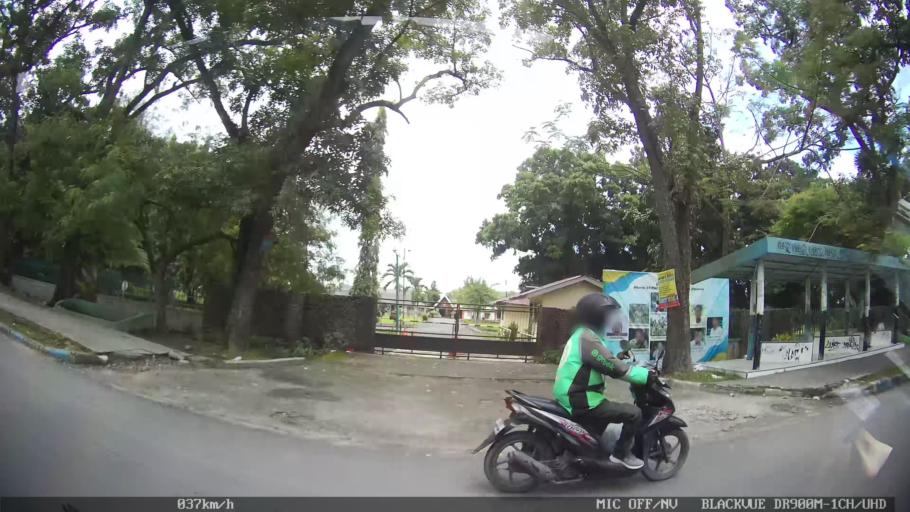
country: ID
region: North Sumatra
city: Medan
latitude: 3.6144
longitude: 98.7110
